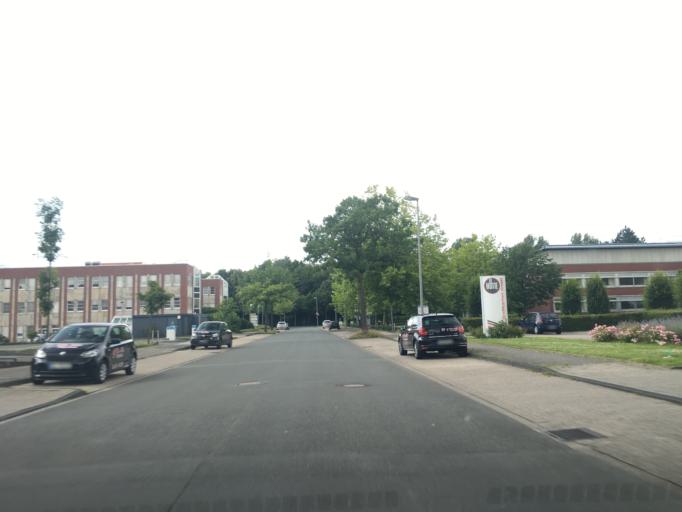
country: DE
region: North Rhine-Westphalia
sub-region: Regierungsbezirk Munster
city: Muenster
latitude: 51.9235
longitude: 7.6586
